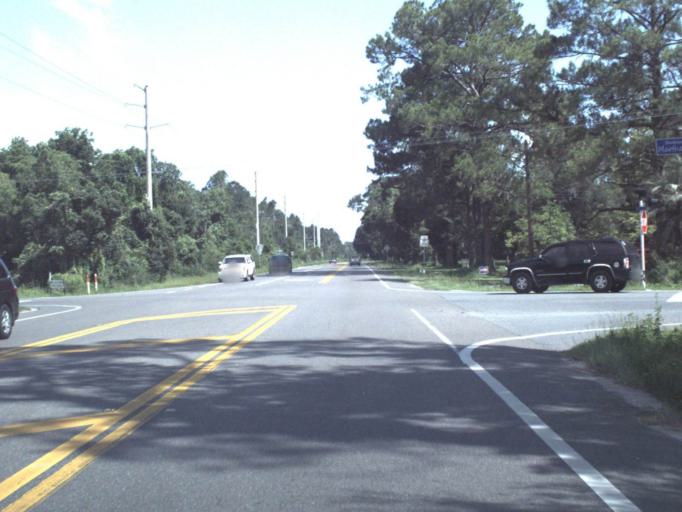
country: US
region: Florida
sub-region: Bradford County
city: Starke
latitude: 29.9277
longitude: -82.1010
